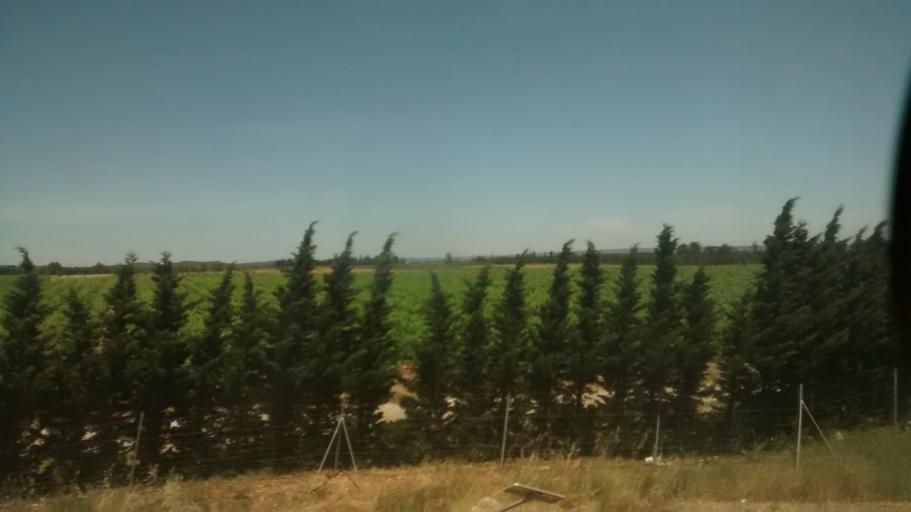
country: FR
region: Languedoc-Roussillon
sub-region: Departement du Gard
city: Jonquieres-Saint-Vincent
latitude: 43.8439
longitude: 4.5521
